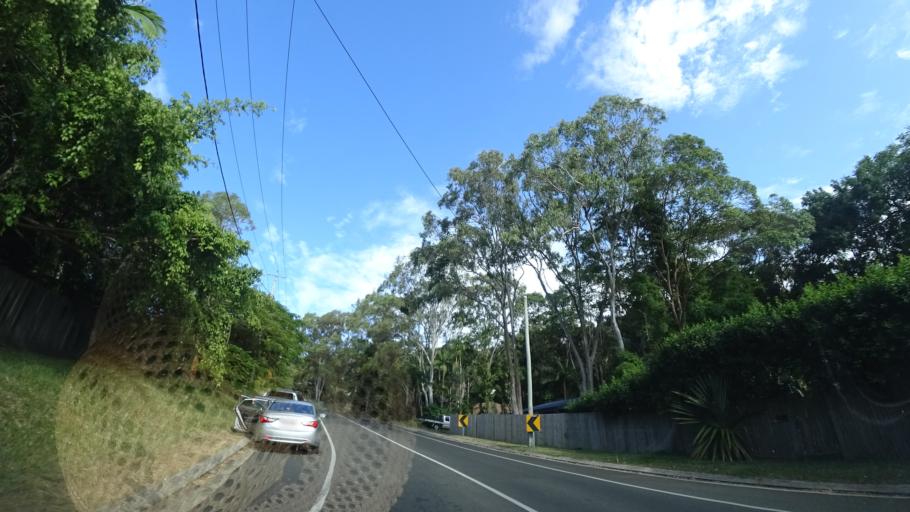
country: AU
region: Queensland
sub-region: Sunshine Coast
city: Coolum Beach
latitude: -26.5569
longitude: 153.0810
